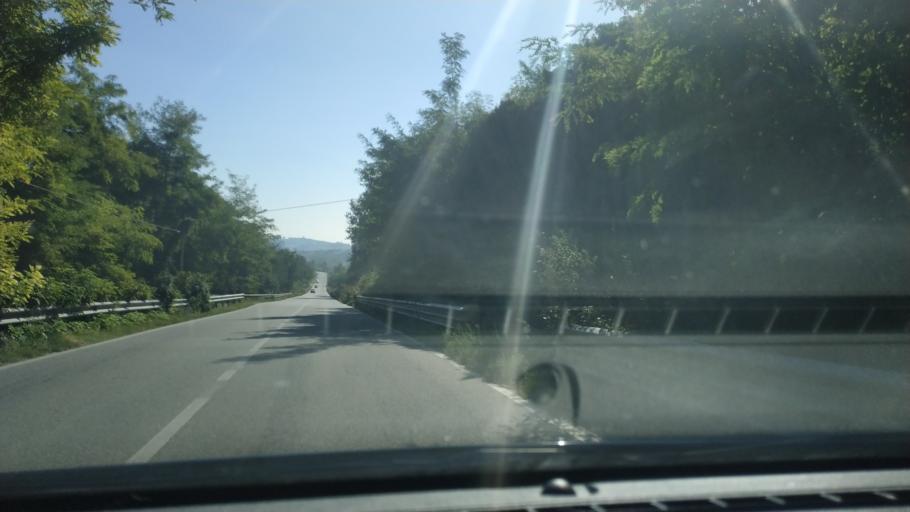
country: IT
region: Piedmont
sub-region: Provincia di Alessandria
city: Ozzano Monferrato
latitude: 45.1071
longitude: 8.3894
